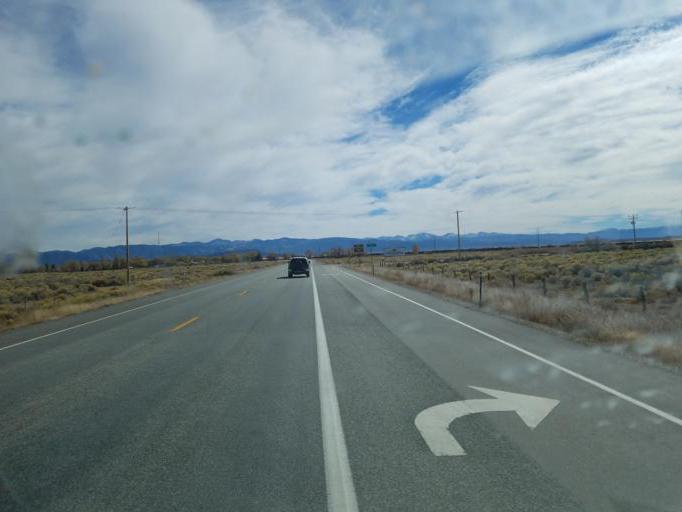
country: US
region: Colorado
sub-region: Costilla County
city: San Luis
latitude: 37.4384
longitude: -105.5235
